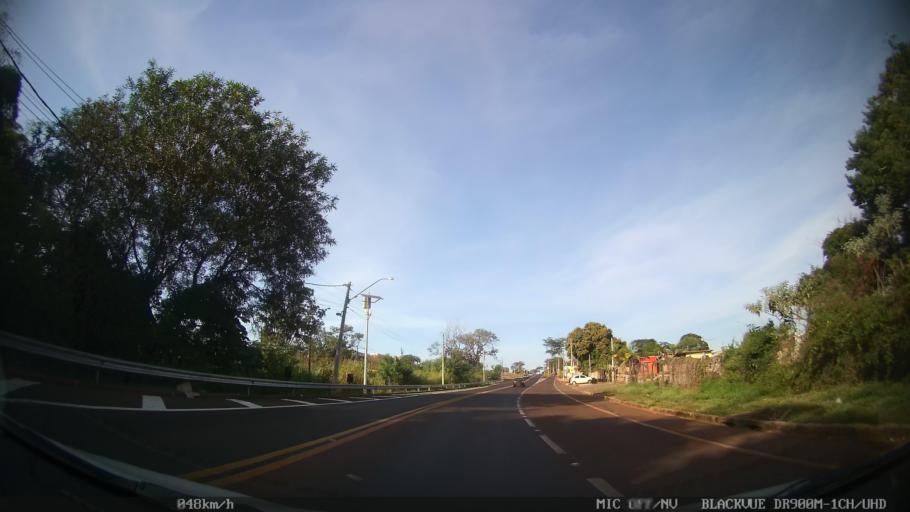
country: BR
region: Sao Paulo
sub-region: Ribeirao Preto
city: Ribeirao Preto
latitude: -21.2688
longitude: -47.8172
